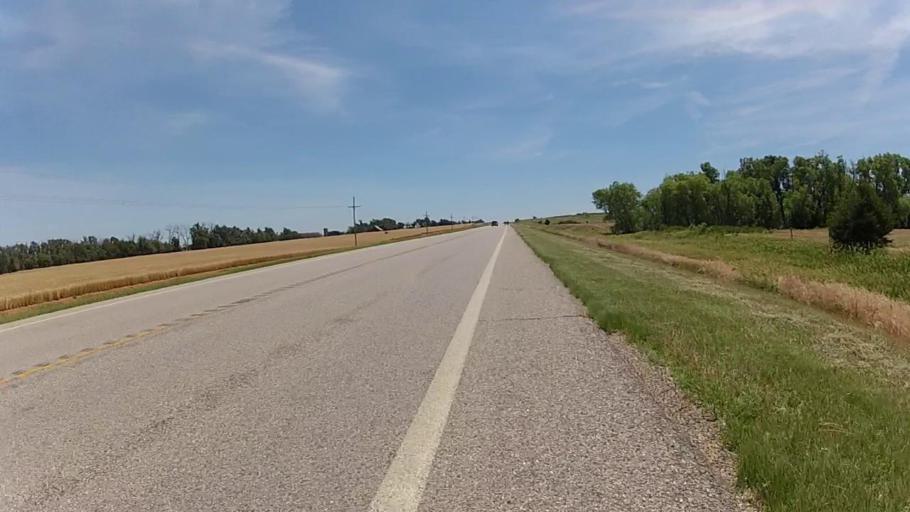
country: US
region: Kansas
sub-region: Barber County
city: Medicine Lodge
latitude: 37.2538
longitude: -98.4843
